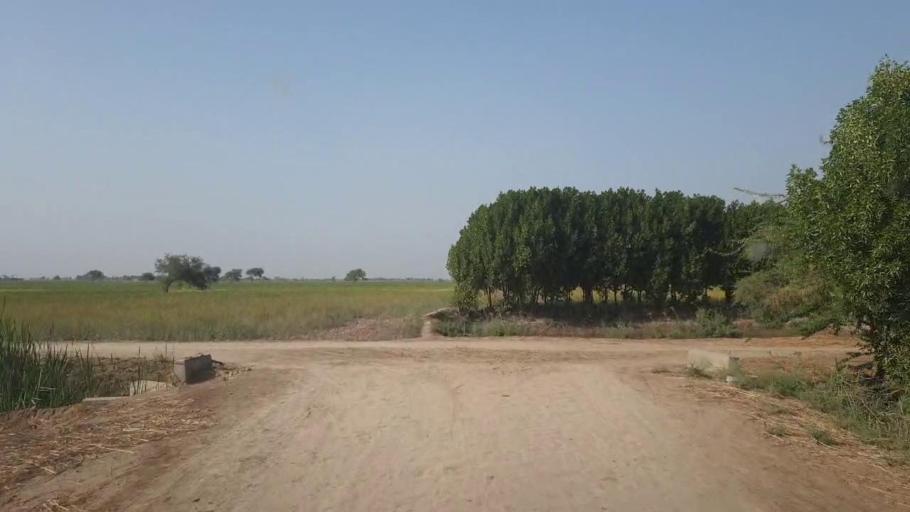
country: PK
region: Sindh
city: Kario
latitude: 24.5819
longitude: 68.5441
